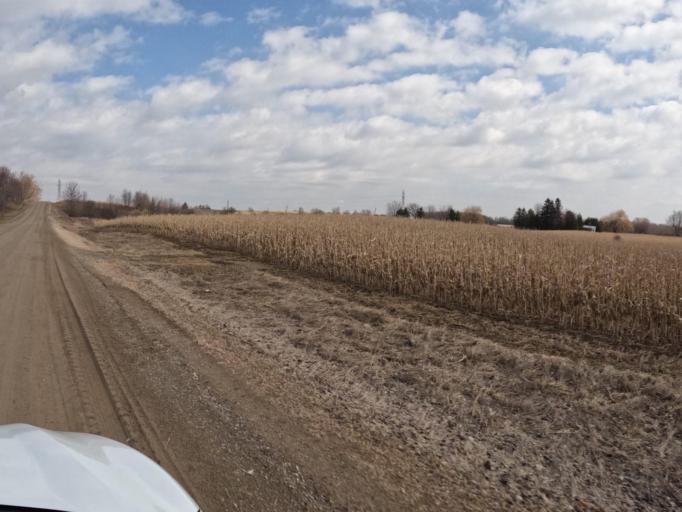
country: CA
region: Ontario
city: Orangeville
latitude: 43.9360
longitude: -80.2428
